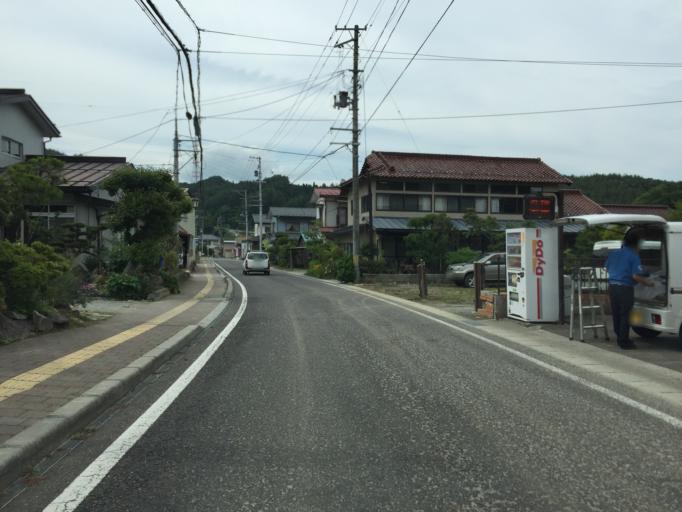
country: JP
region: Fukushima
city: Namie
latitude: 37.4362
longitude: 140.7951
